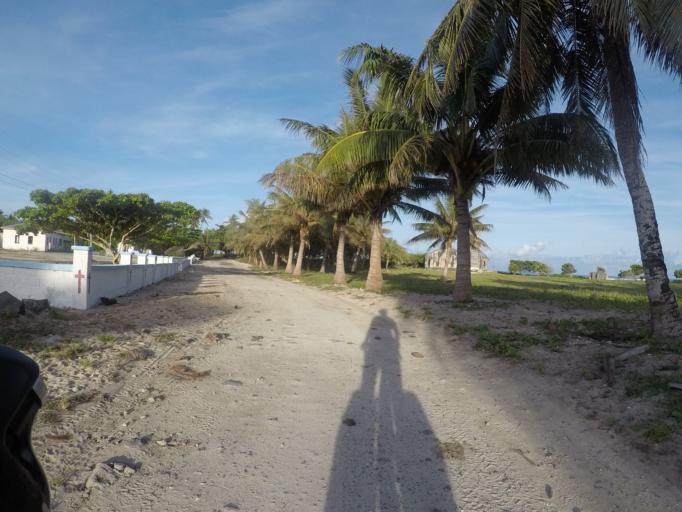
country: WS
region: Vaisigano
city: Asau
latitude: -13.4943
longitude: -172.7829
